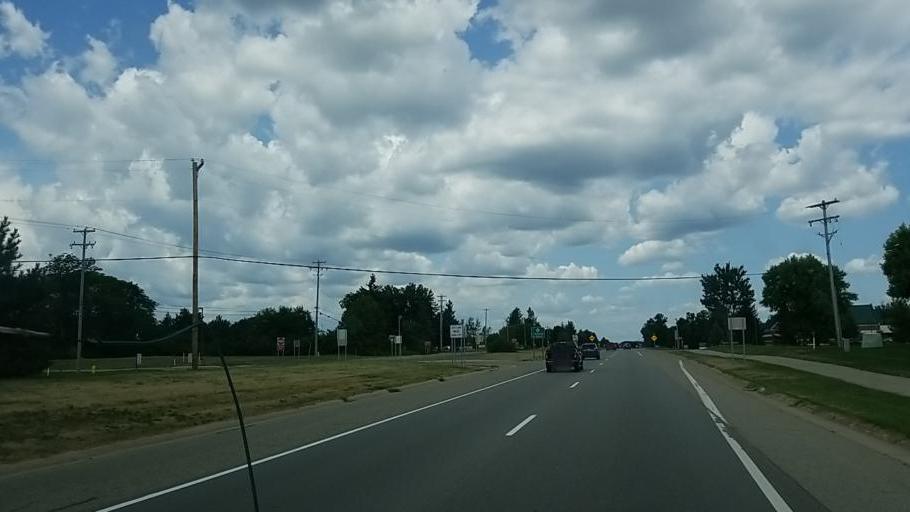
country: US
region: Michigan
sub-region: Kent County
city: East Grand Rapids
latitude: 42.9919
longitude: -85.5902
